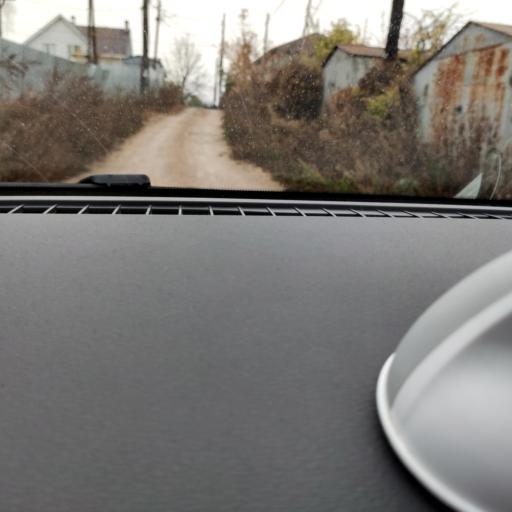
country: RU
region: Samara
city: Samara
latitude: 53.2700
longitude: 50.2132
